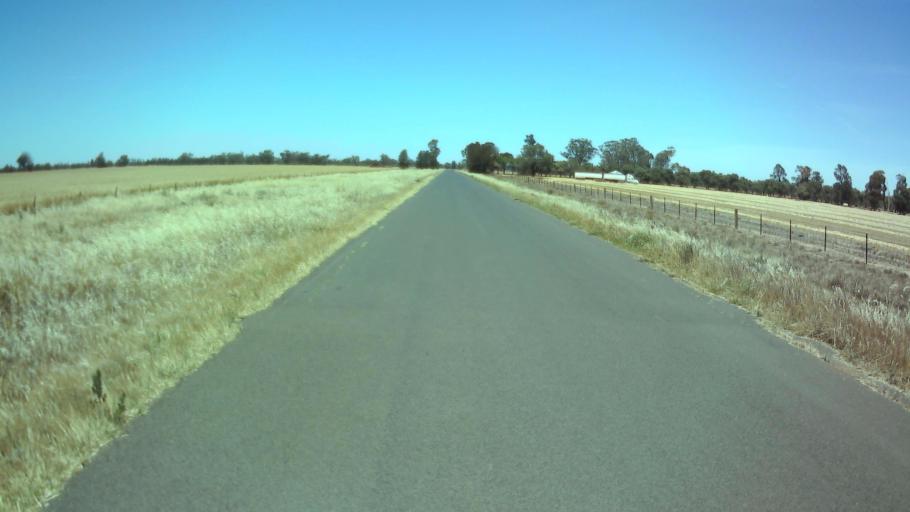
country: AU
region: New South Wales
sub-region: Weddin
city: Grenfell
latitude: -34.0283
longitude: 147.7912
